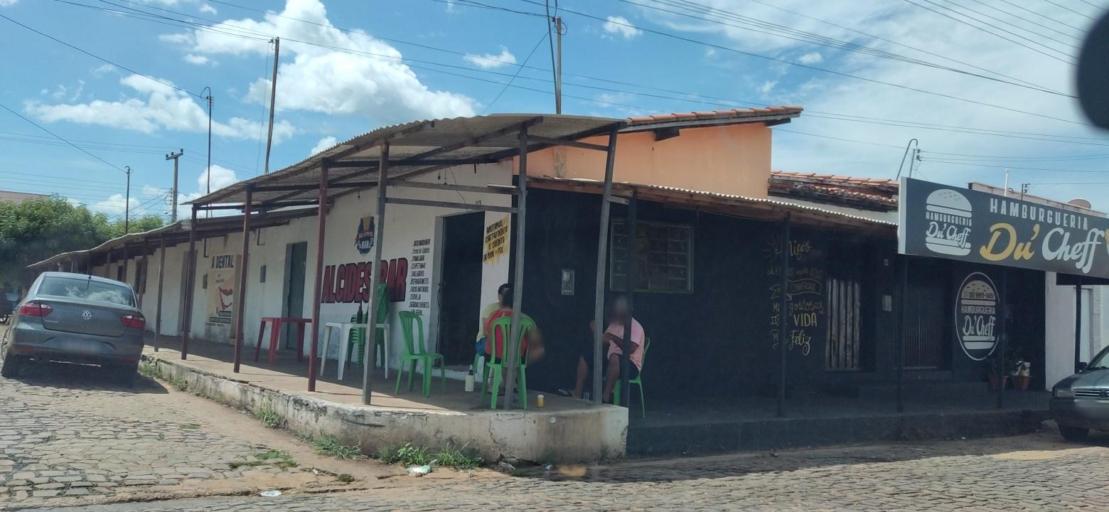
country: BR
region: Piaui
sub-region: Valenca Do Piaui
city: Valenca do Piaui
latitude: -6.4090
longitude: -41.7451
